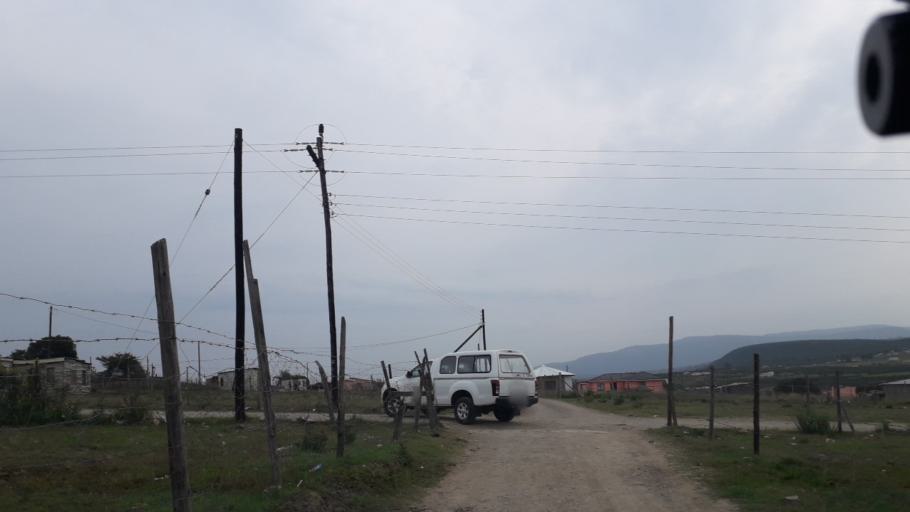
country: ZA
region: Eastern Cape
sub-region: Buffalo City Metropolitan Municipality
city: Bhisho
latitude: -32.8353
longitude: 27.3696
